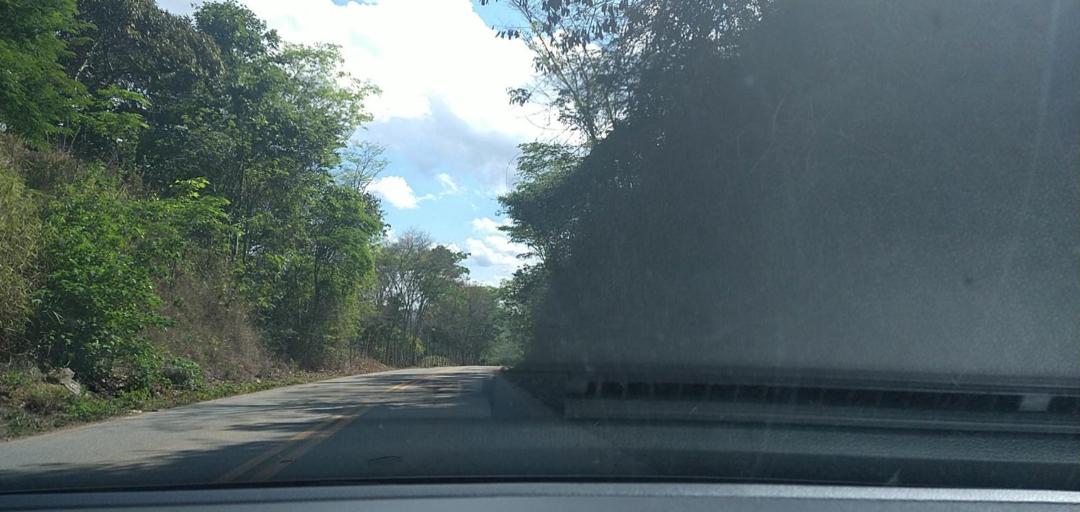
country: BR
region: Minas Gerais
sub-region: Alvinopolis
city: Alvinopolis
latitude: -20.0446
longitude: -43.0334
